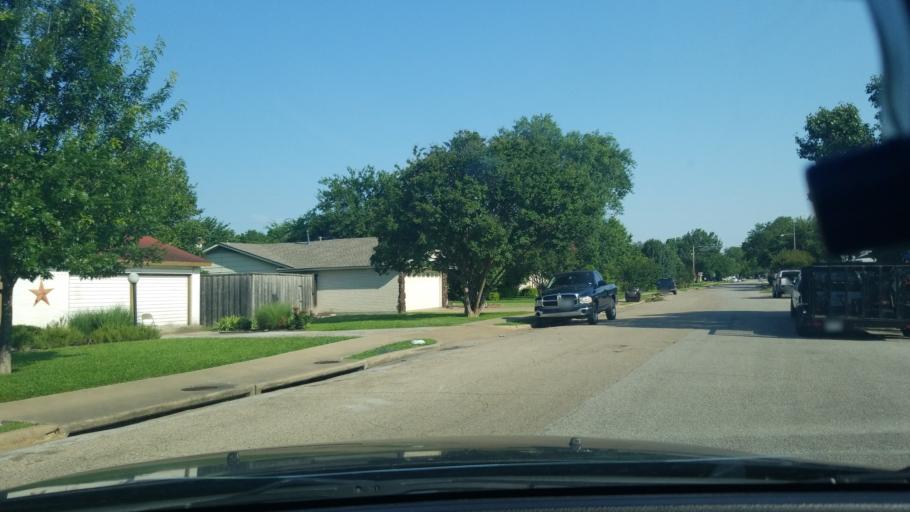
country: US
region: Texas
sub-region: Dallas County
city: Mesquite
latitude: 32.8254
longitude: -96.6375
